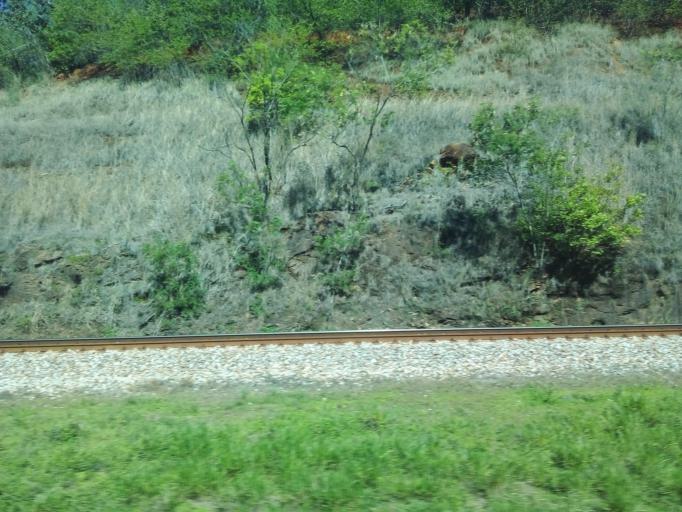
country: BR
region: Minas Gerais
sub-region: Governador Valadares
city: Governador Valadares
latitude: -18.8509
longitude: -41.8608
